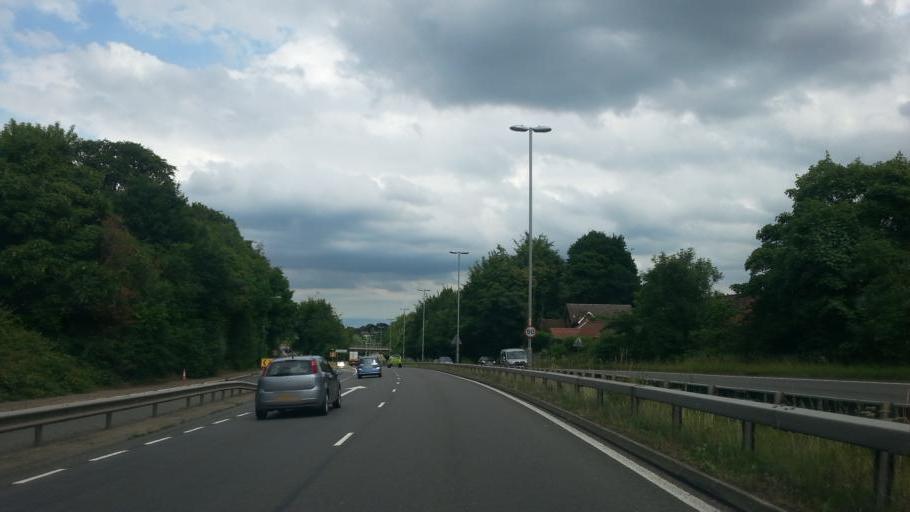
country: GB
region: England
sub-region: Norfolk
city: Cringleford
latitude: 52.6047
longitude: 1.2393
